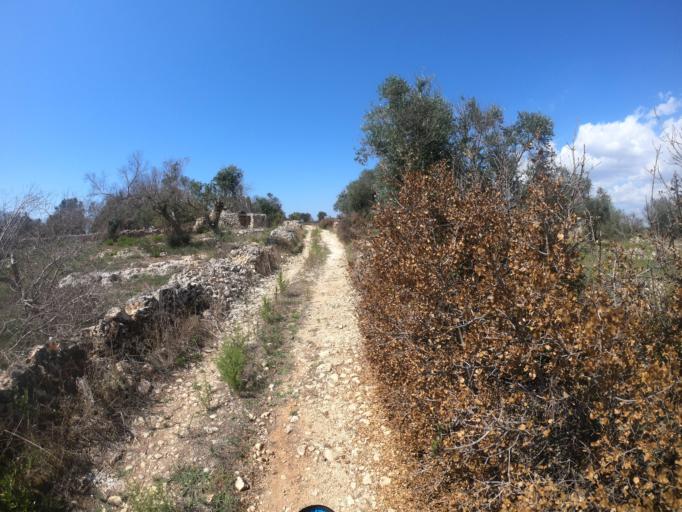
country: IT
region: Apulia
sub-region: Provincia di Lecce
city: Secli
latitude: 40.1201
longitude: 18.0808
